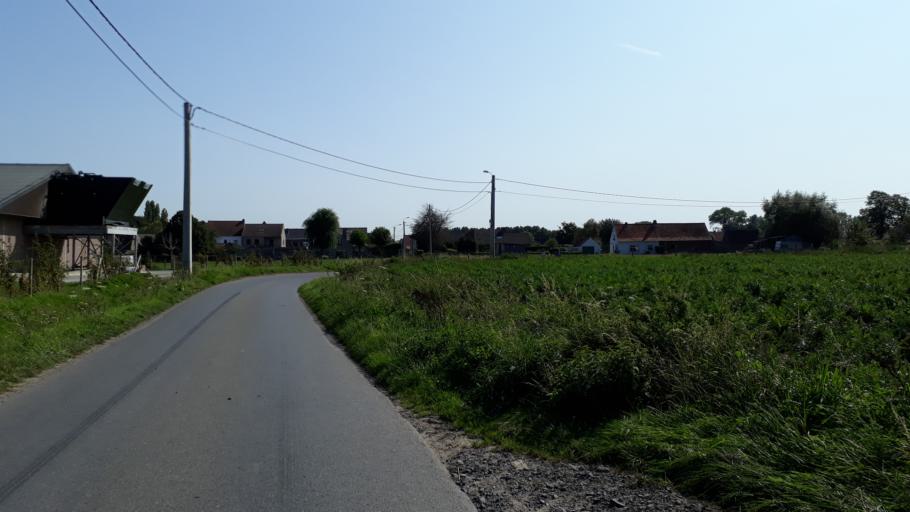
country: BE
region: Flanders
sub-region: Provincie West-Vlaanderen
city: Torhout
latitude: 51.0667
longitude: 3.0721
